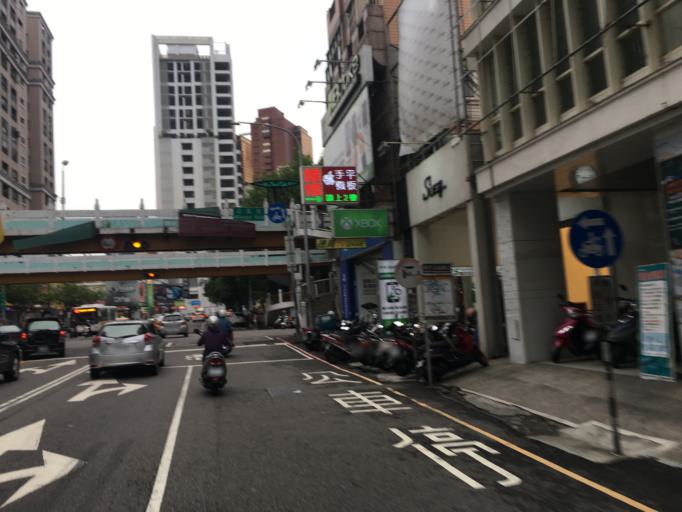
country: TW
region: Taiwan
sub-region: Taichung City
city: Taichung
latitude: 24.1504
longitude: 120.6654
